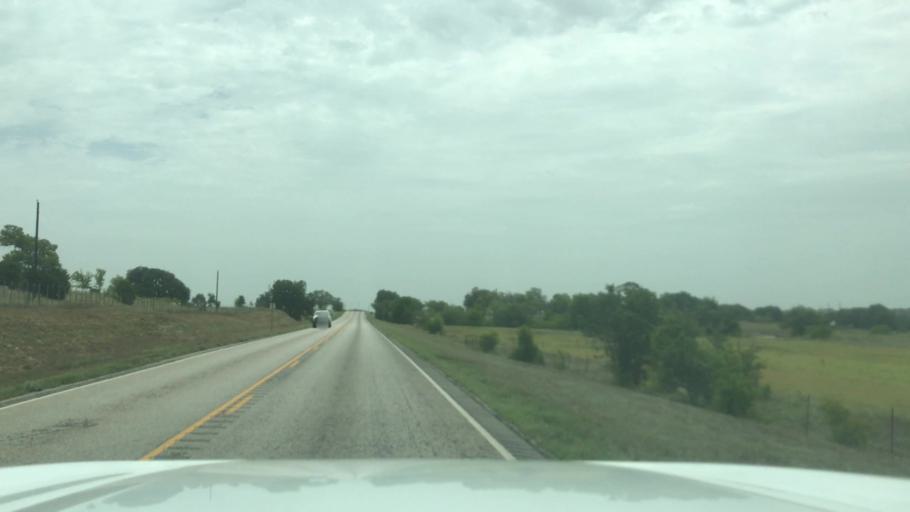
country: US
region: Texas
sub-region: Hamilton County
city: Hico
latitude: 32.0460
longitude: -98.1455
